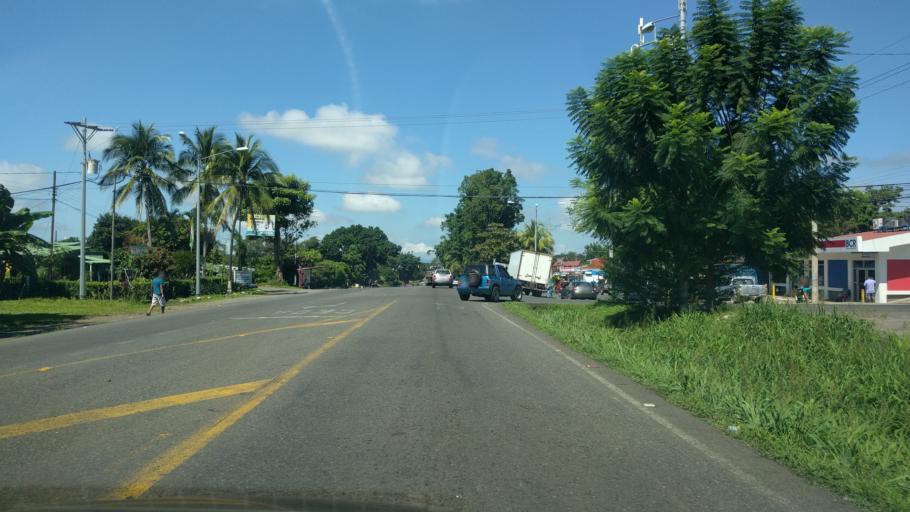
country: CR
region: Puntarenas
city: Esparza
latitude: 9.9973
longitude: -84.6571
